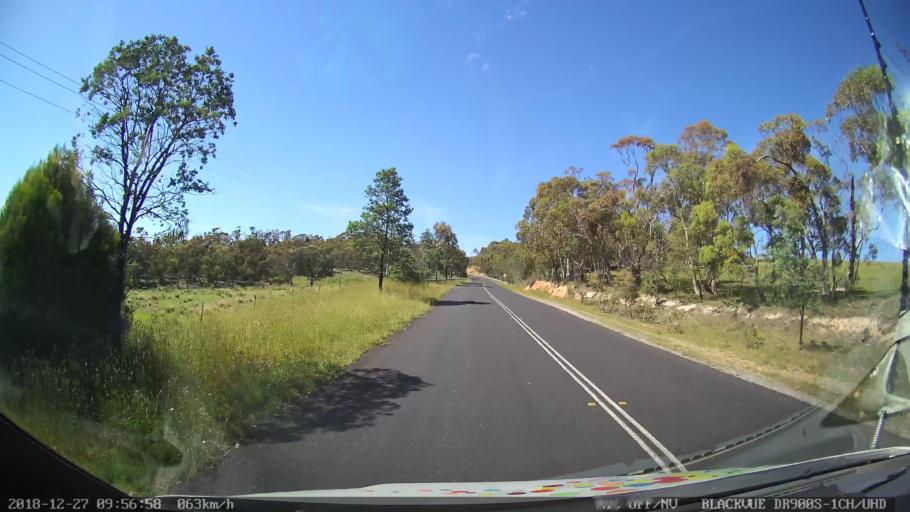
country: AU
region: New South Wales
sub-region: Lithgow
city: Portland
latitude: -33.4174
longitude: 149.9717
